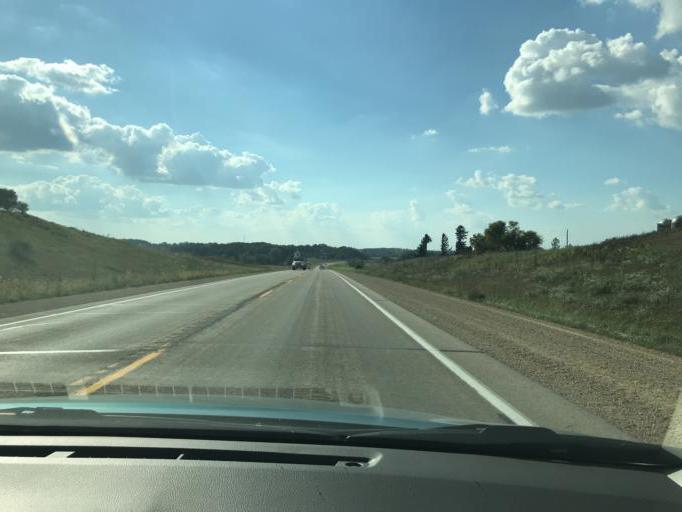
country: US
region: Wisconsin
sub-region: Green County
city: Brodhead
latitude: 42.5885
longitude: -89.4738
